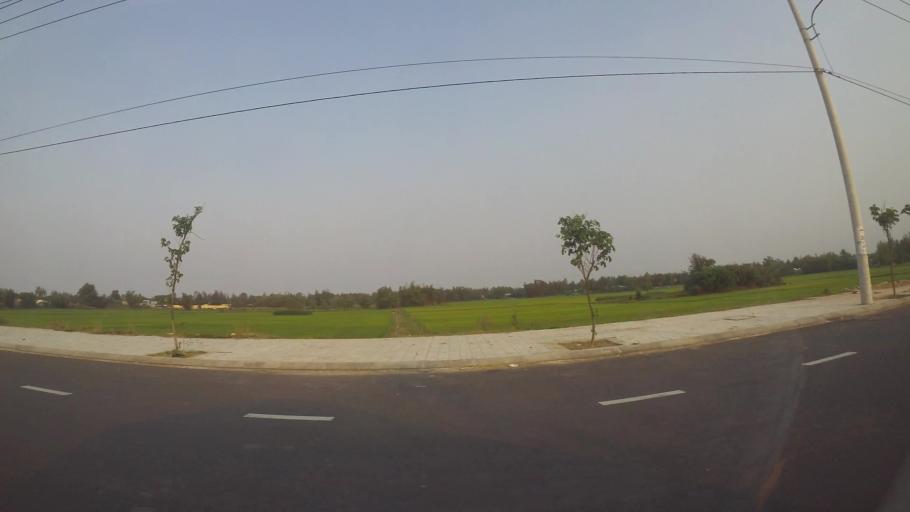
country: VN
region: Da Nang
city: Ngu Hanh Son
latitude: 15.9751
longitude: 108.2328
